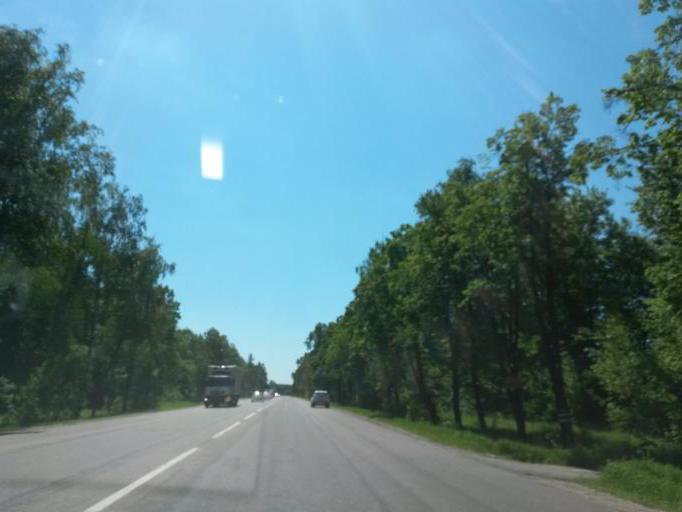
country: RU
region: Moskovskaya
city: Stolbovaya
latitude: 55.2132
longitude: 37.5060
